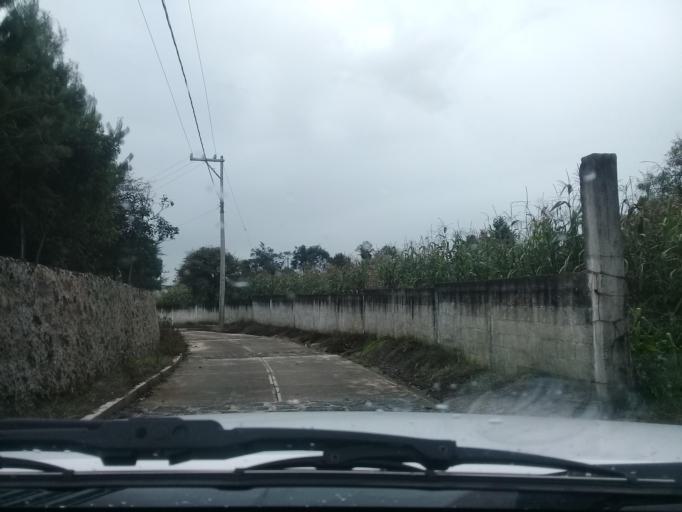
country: MX
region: Veracruz
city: Rafael Lucio
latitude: 19.6162
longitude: -96.9992
